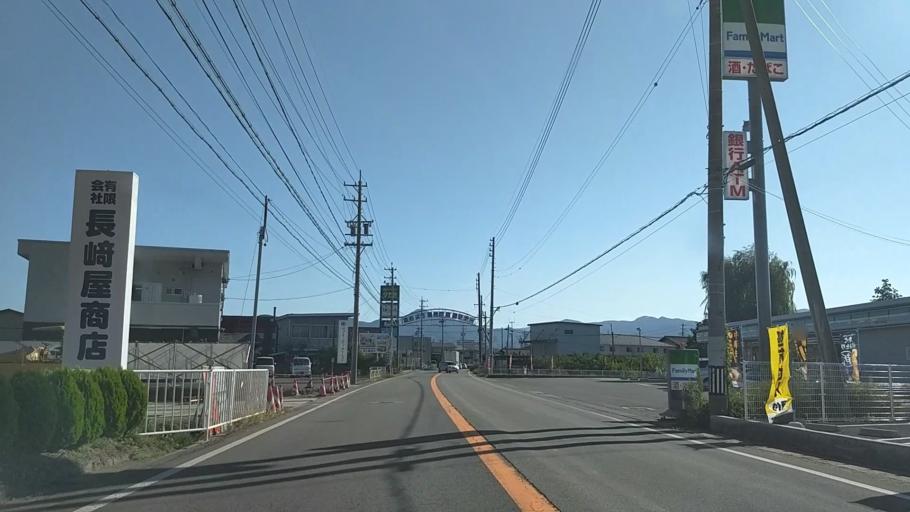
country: JP
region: Nagano
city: Nagano-shi
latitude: 36.5676
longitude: 138.1412
